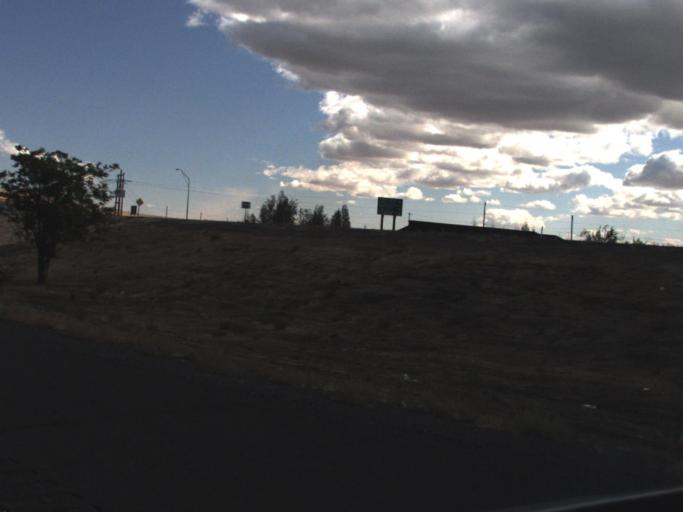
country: US
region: Washington
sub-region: Yakima County
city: Selah
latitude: 46.6232
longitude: -120.5335
